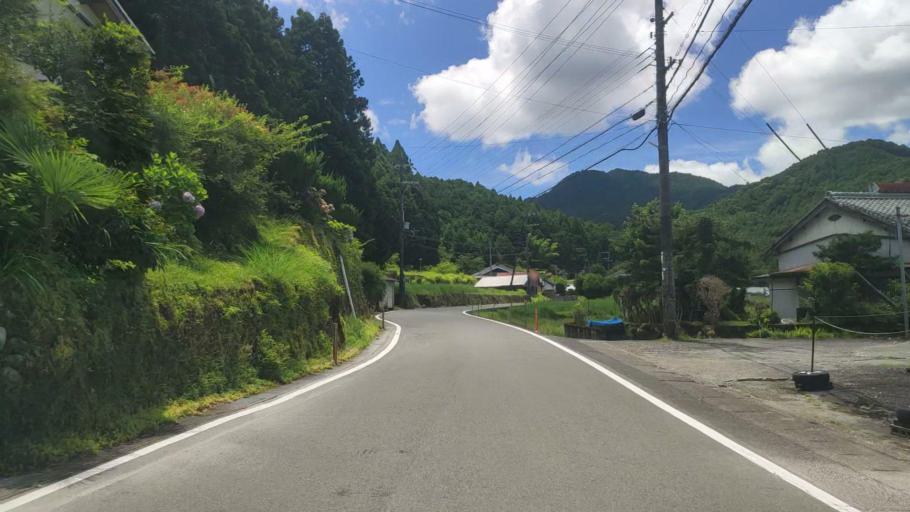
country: JP
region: Mie
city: Owase
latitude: 33.9474
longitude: 136.0765
